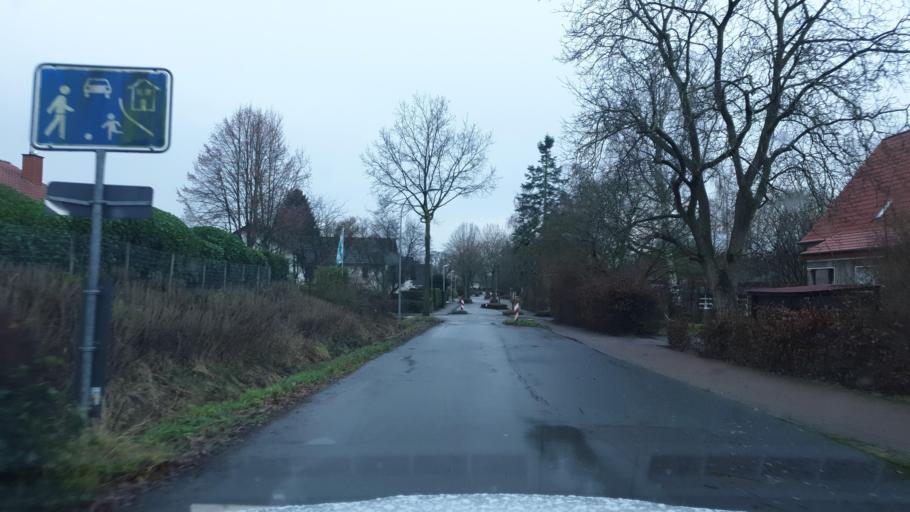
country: DE
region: North Rhine-Westphalia
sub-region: Regierungsbezirk Detmold
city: Hille
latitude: 52.2586
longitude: 8.7496
